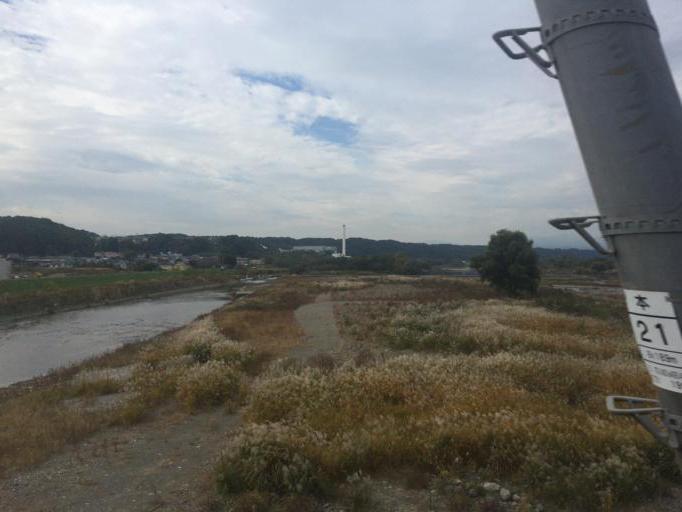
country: JP
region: Tokyo
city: Hino
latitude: 35.6938
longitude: 139.3631
